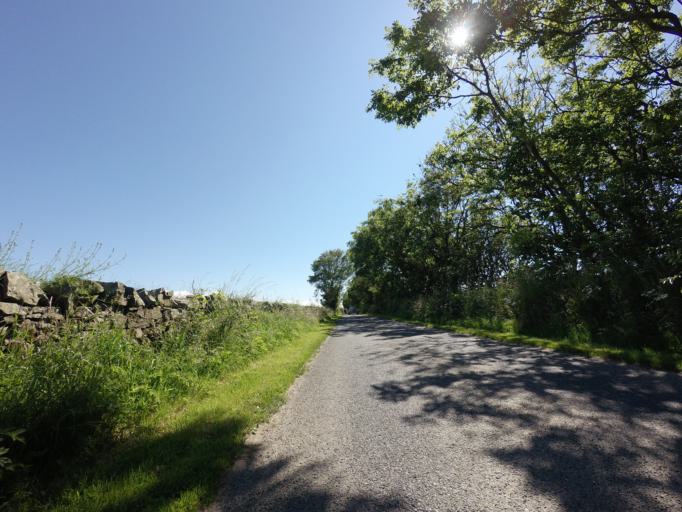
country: GB
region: Scotland
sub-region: Aberdeenshire
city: Macduff
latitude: 57.6569
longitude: -2.4989
